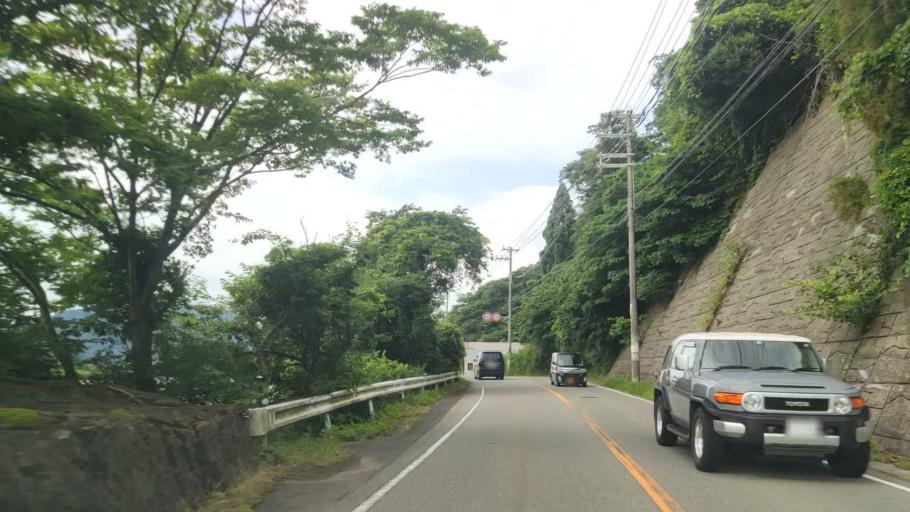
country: JP
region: Hyogo
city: Toyooka
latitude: 35.6379
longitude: 134.8217
